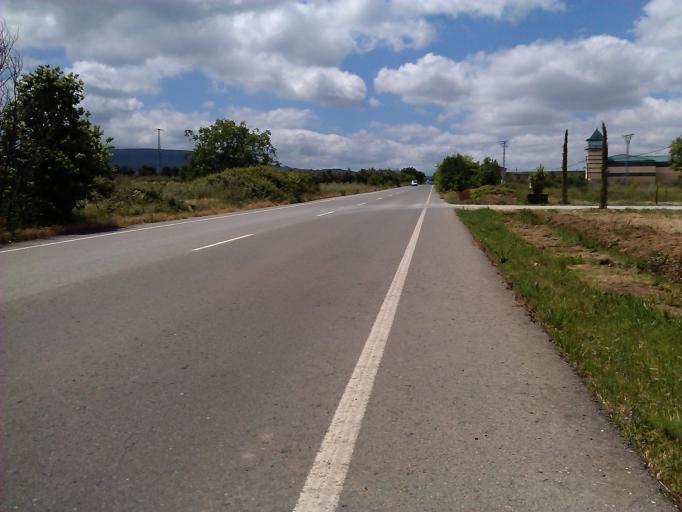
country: ES
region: La Rioja
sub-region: Provincia de La Rioja
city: Navarrete
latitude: 42.4253
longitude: -2.5789
